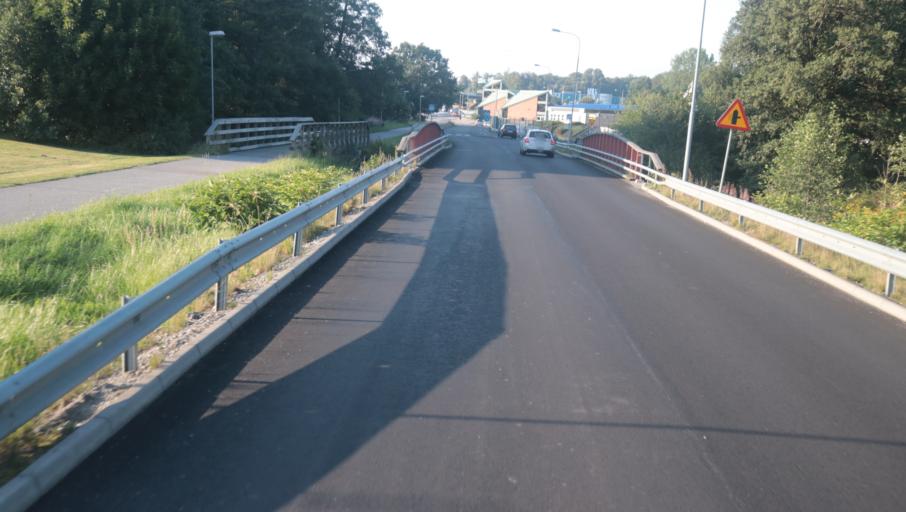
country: SE
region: Blekinge
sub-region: Karlshamns Kommun
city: Karlshamn
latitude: 56.1842
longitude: 14.8479
